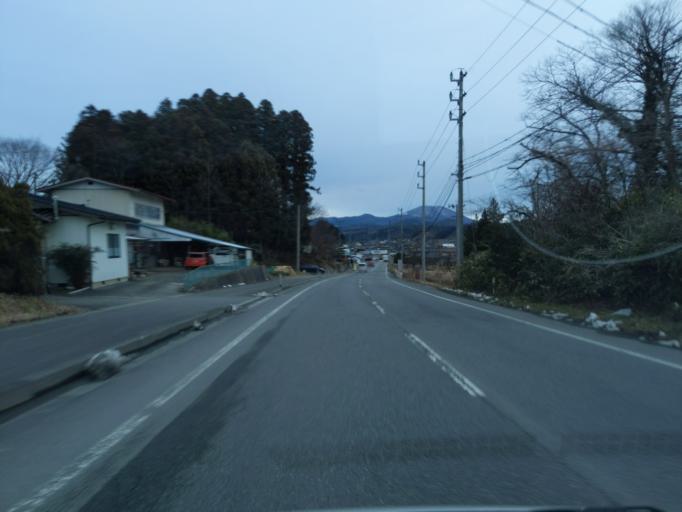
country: JP
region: Iwate
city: Ichinoseki
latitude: 39.0231
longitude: 141.3246
